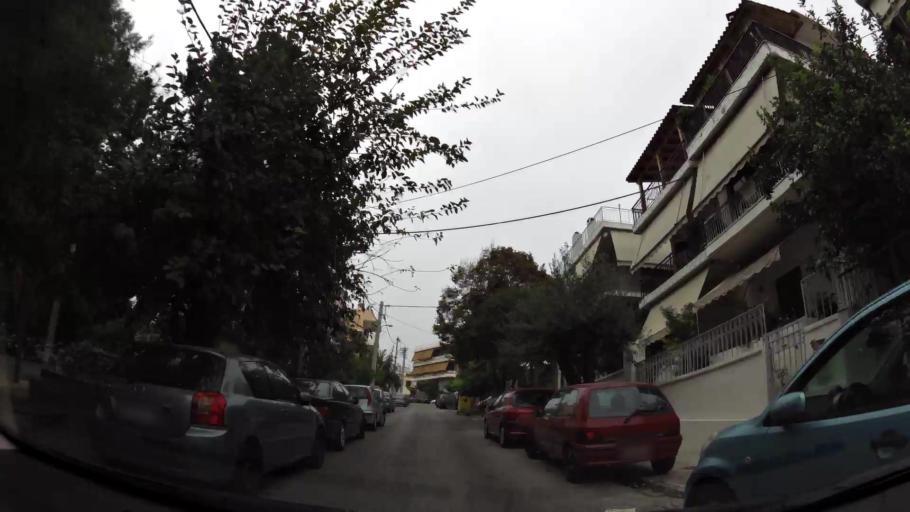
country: GR
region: Attica
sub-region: Nomarchia Athinas
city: Agia Varvara
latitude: 37.9981
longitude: 23.6673
